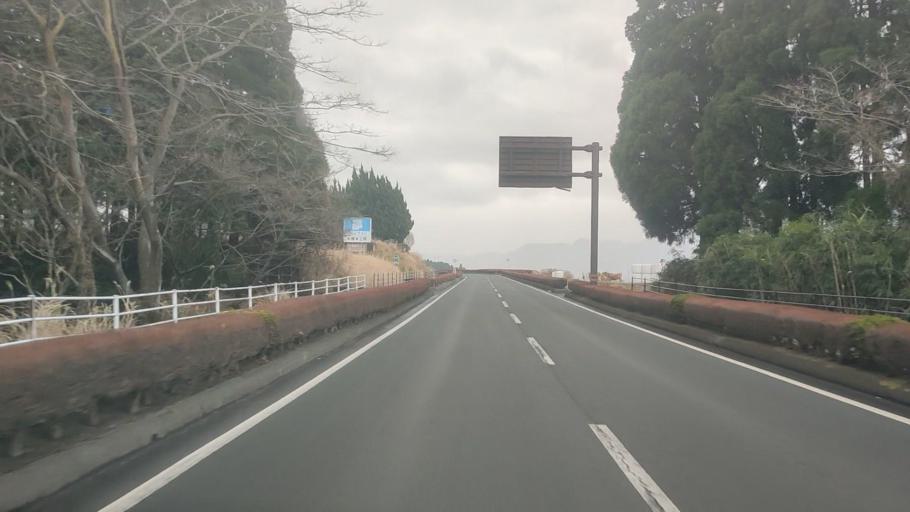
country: JP
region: Kumamoto
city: Aso
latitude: 32.8330
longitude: 131.0734
